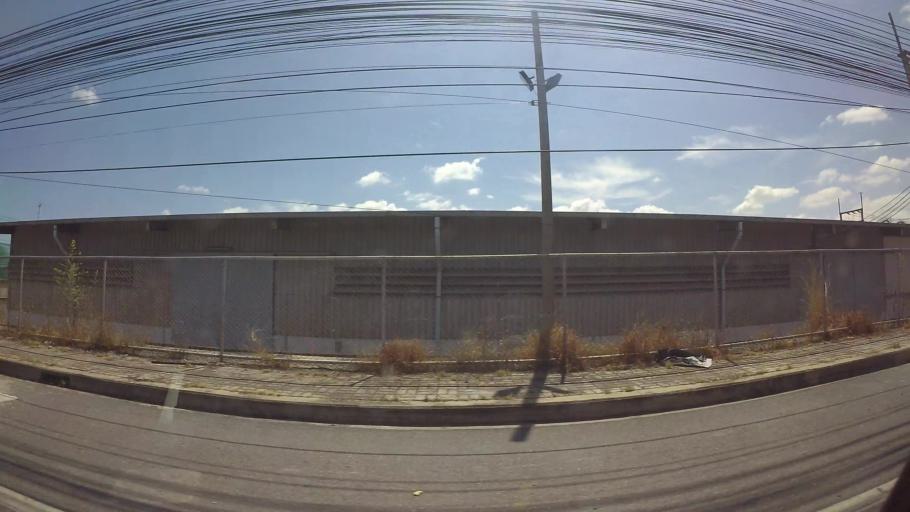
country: TH
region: Chon Buri
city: Bang Lamung
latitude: 13.1088
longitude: 100.9346
